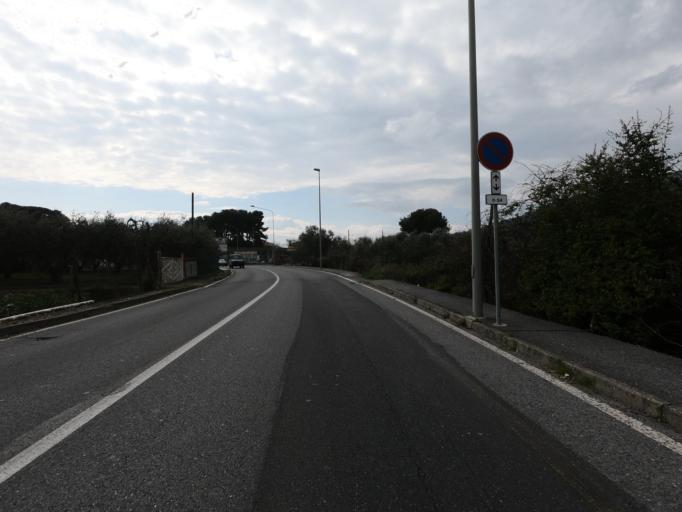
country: IT
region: Liguria
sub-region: Provincia di Savona
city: Andora
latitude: 43.9632
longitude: 8.1420
